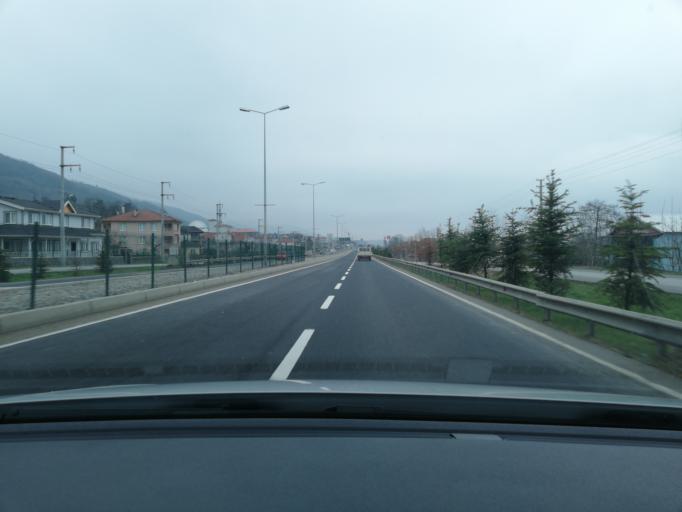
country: TR
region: Duzce
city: Kaynasli
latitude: 40.7727
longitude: 31.3285
